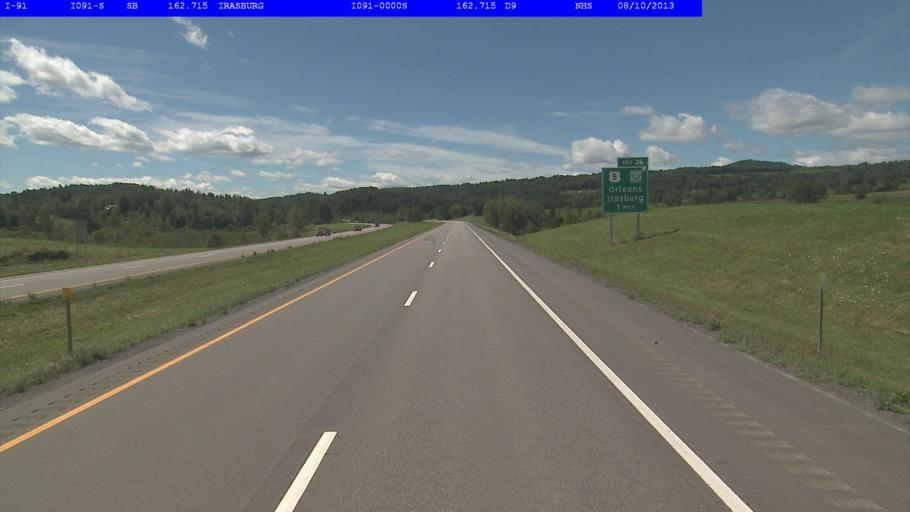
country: US
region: Vermont
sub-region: Orleans County
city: Newport
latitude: 44.8245
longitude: -72.2062
